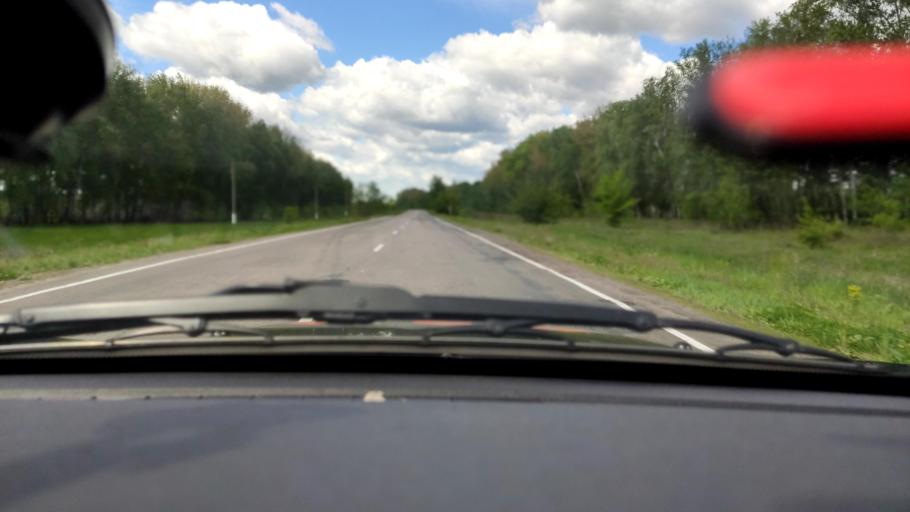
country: RU
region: Belgorod
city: Krasnoye
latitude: 51.0559
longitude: 38.9033
